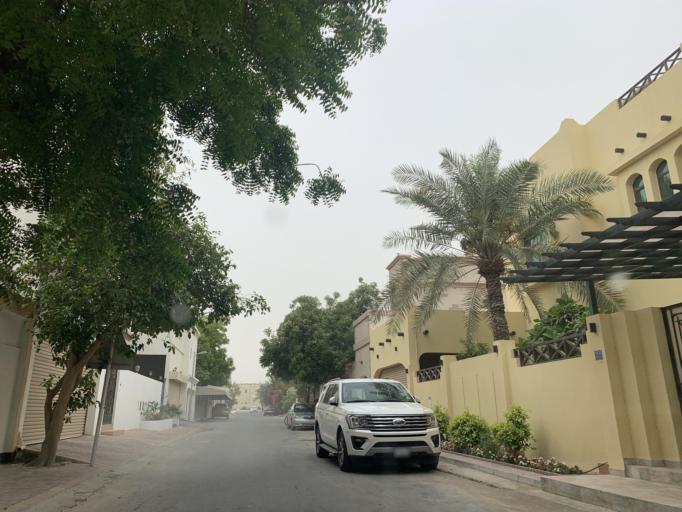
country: BH
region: Northern
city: Ar Rifa'
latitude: 26.1467
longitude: 50.5290
